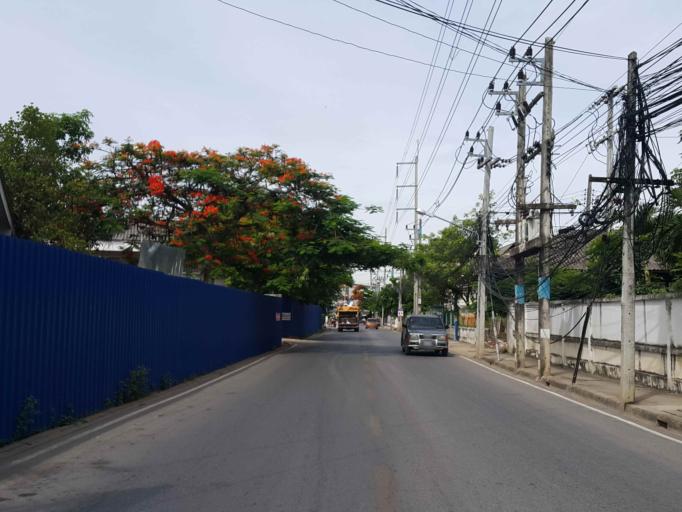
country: TH
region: Chiang Mai
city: Chiang Mai
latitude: 18.7749
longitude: 98.9957
